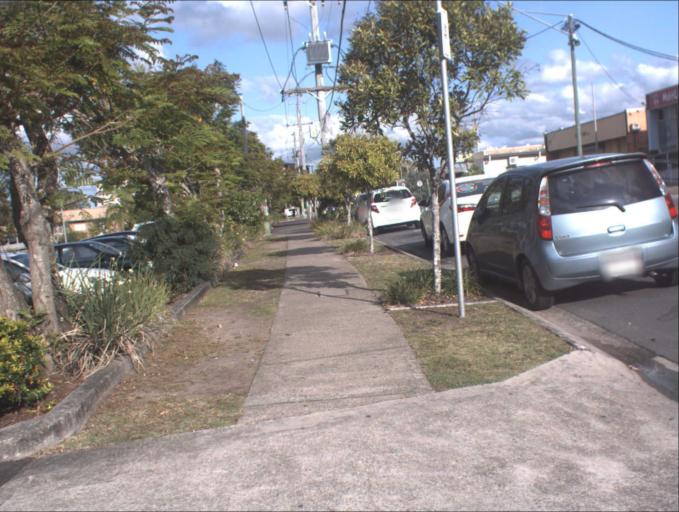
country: AU
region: Queensland
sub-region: Logan
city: Woodridge
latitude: -27.6365
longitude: 153.1037
